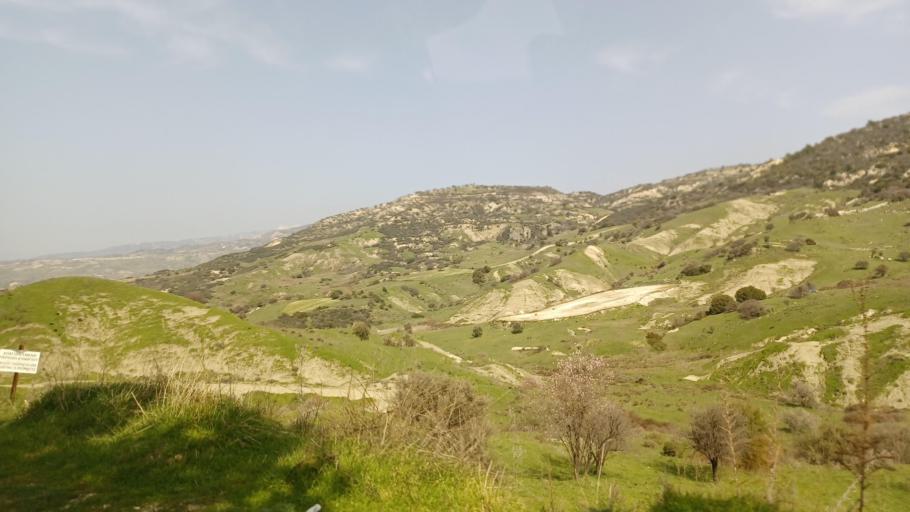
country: CY
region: Limassol
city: Pissouri
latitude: 34.7479
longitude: 32.6629
